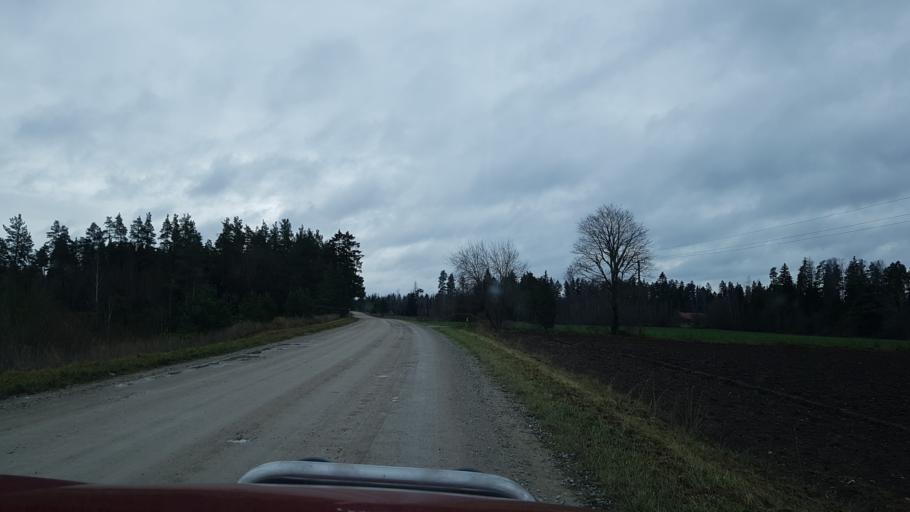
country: EE
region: Paernumaa
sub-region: Halinga vald
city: Parnu-Jaagupi
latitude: 58.5805
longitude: 24.4058
